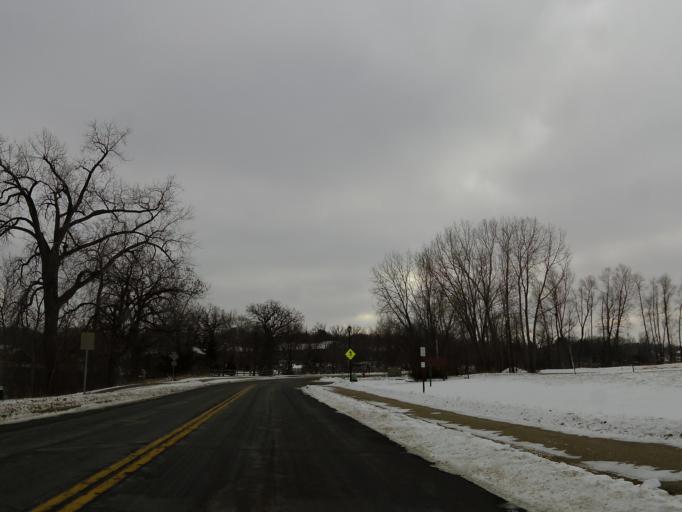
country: US
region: Minnesota
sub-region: Hennepin County
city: Shorewood
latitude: 44.8785
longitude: -93.6203
